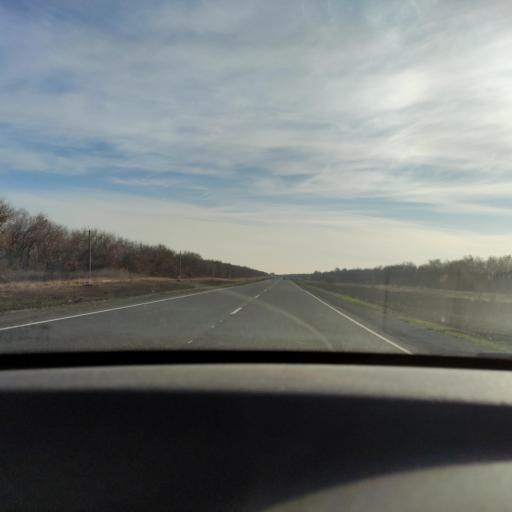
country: RU
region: Samara
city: Krasnoarmeyskoye
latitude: 52.8020
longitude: 50.0142
